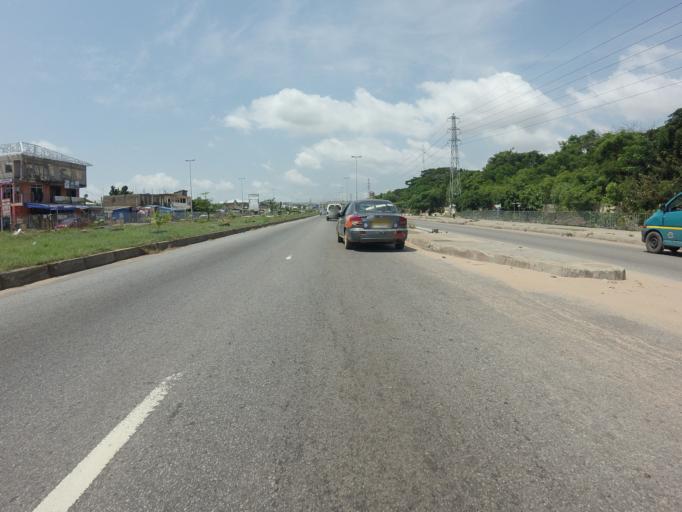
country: GH
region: Greater Accra
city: Gbawe
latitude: 5.5903
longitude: -0.2847
